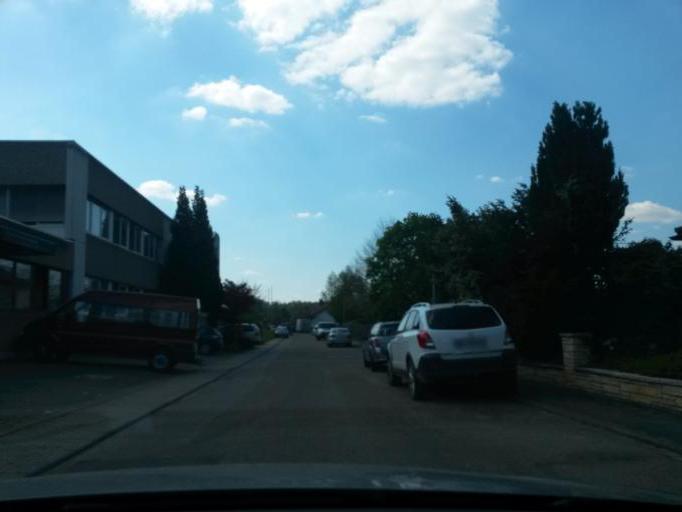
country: DE
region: Baden-Wuerttemberg
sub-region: Karlsruhe Region
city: Birkenfeld
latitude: 48.8903
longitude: 8.6132
